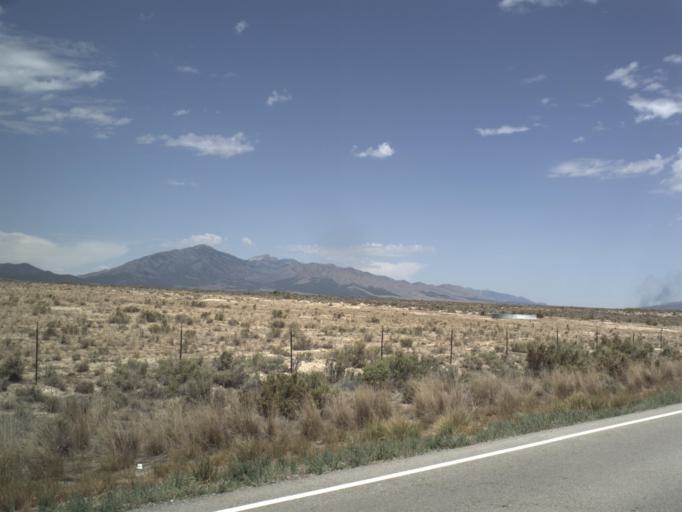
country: US
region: Utah
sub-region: Tooele County
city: Tooele
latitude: 40.2127
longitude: -112.4069
